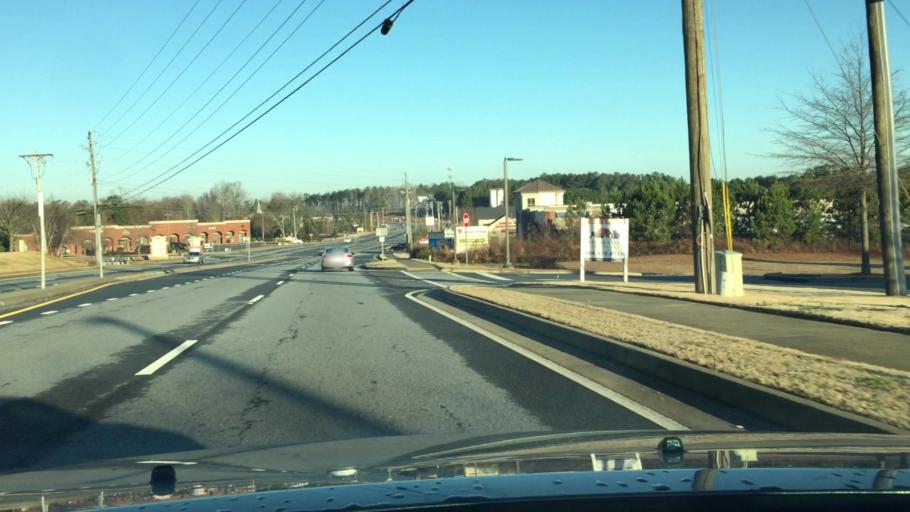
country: US
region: Georgia
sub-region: Forsyth County
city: Cumming
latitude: 34.1648
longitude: -84.1768
